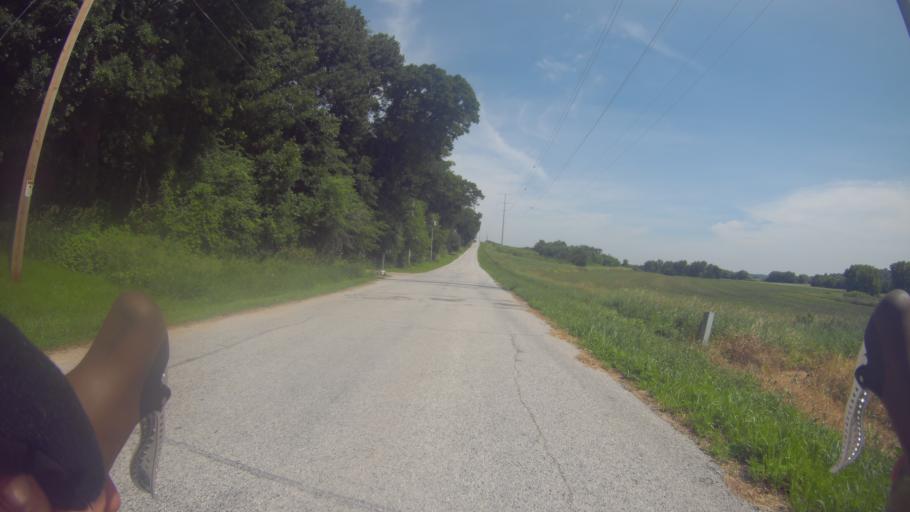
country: US
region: Wisconsin
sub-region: Dane County
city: Deerfield
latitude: 43.0488
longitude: -89.0412
